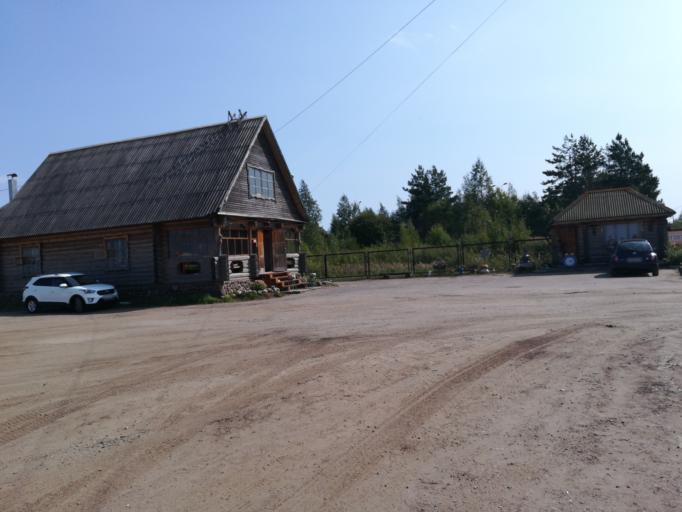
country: RU
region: Smolensk
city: Velizh
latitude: 55.5902
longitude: 31.2374
